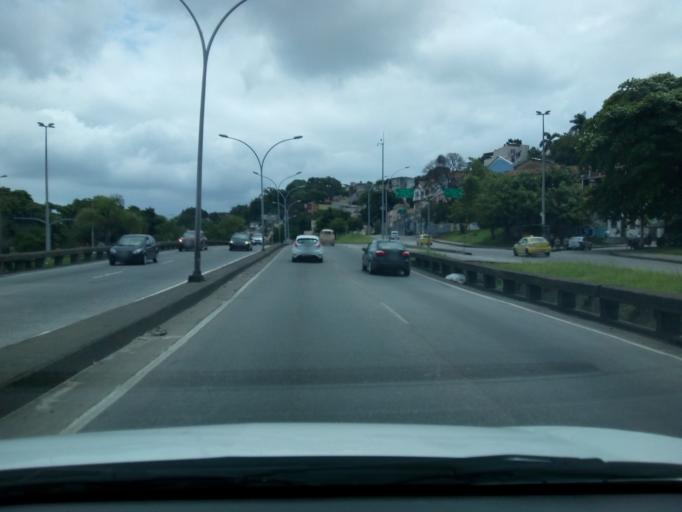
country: BR
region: Rio de Janeiro
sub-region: Rio De Janeiro
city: Rio de Janeiro
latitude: -22.9180
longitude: -43.1945
